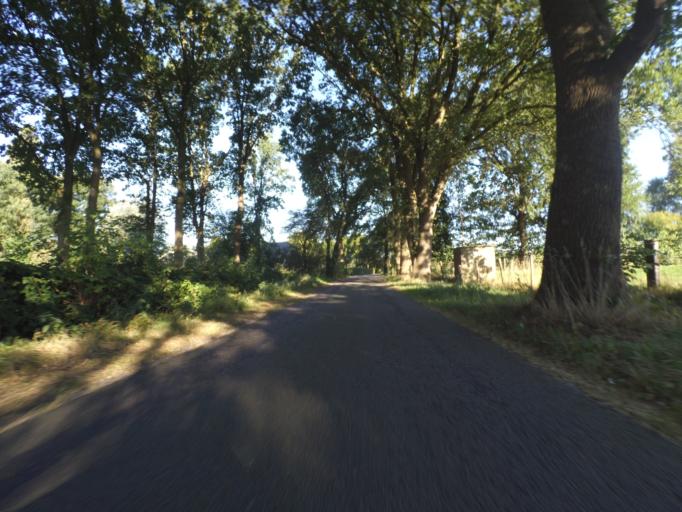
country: NL
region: Gelderland
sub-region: Gemeente Barneveld
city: Barneveld
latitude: 52.1754
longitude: 5.5622
